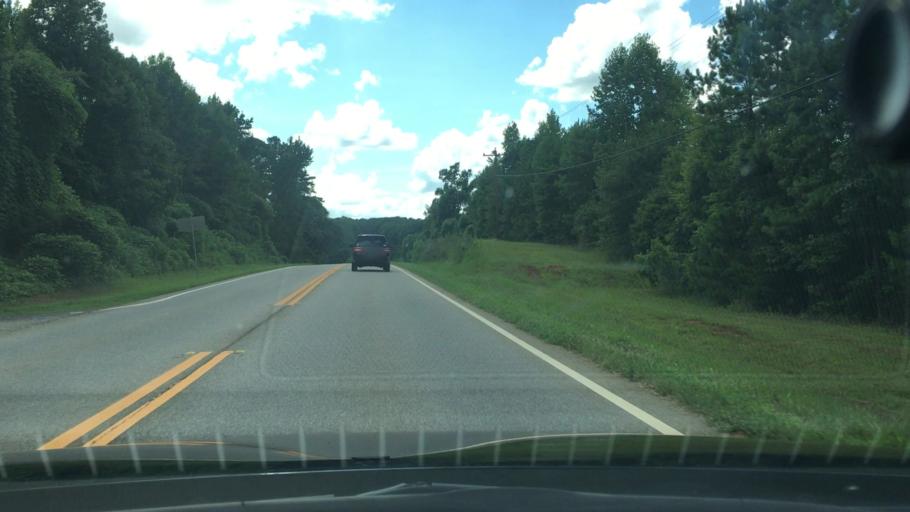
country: US
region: Georgia
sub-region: Putnam County
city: Eatonton
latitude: 33.3154
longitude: -83.4314
